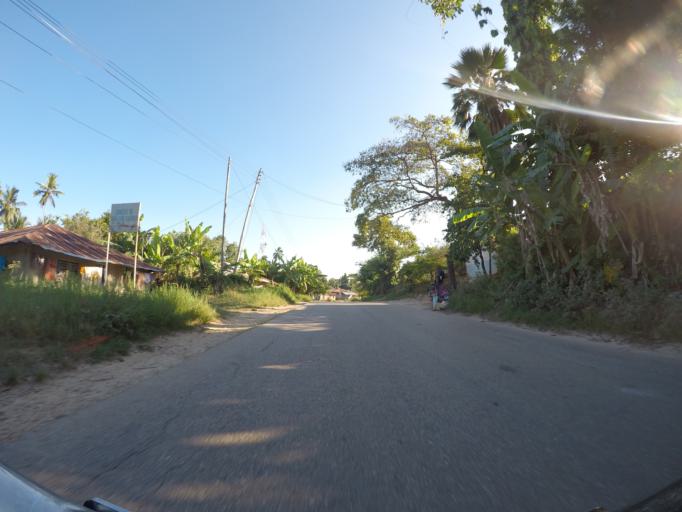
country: TZ
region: Pemba South
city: Chake Chake
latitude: -5.2952
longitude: 39.7595
